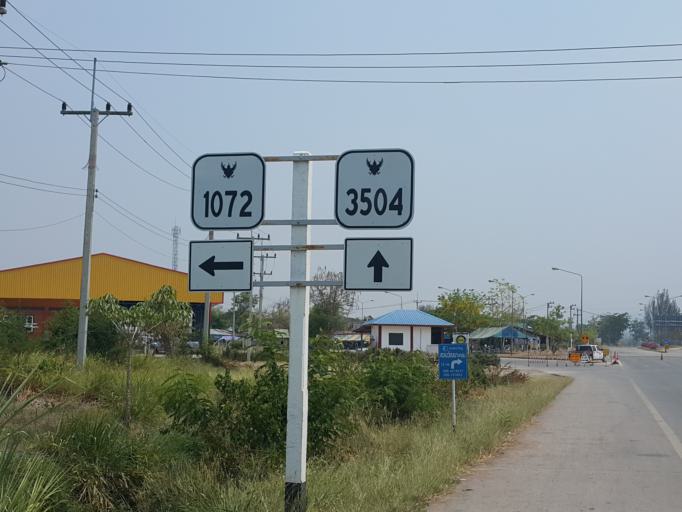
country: TH
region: Nakhon Sawan
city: Mae Wong
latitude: 15.8993
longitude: 99.4709
